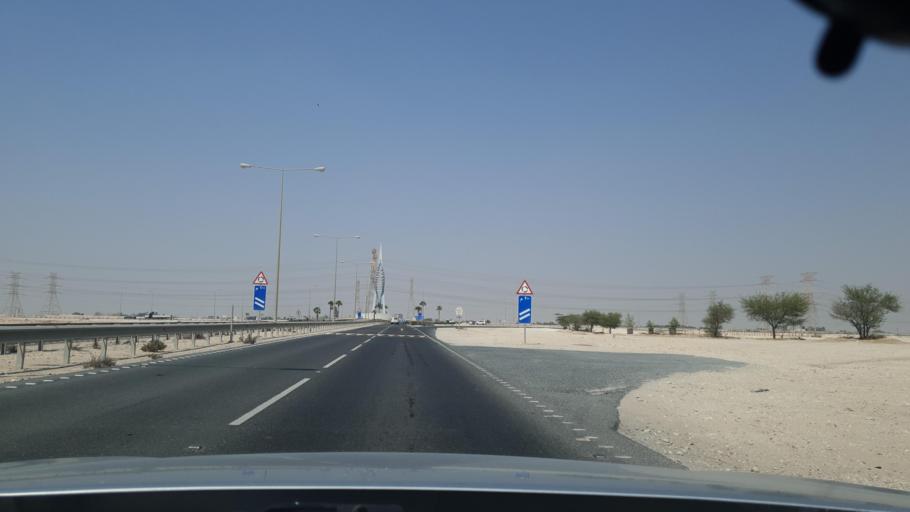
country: QA
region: Al Khawr
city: Al Khawr
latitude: 25.7517
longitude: 51.4771
